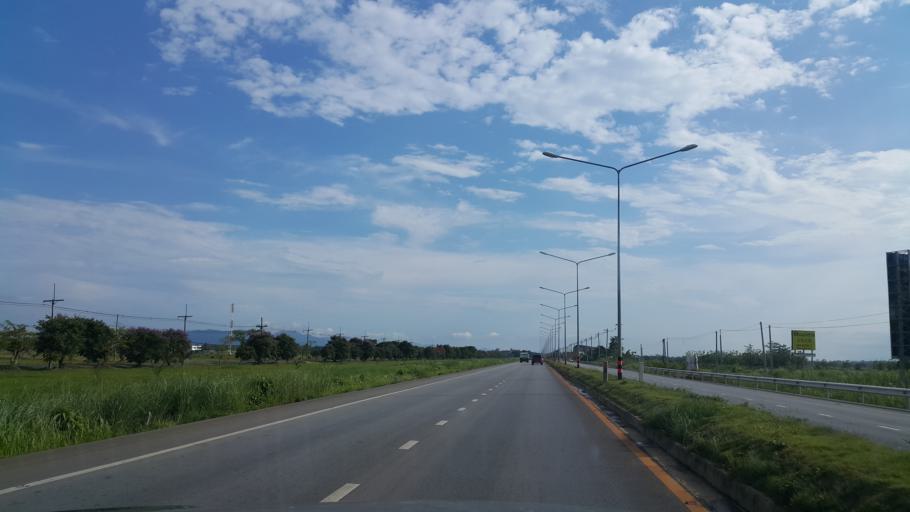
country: TH
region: Chiang Rai
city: Chiang Rai
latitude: 19.9476
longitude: 99.8728
